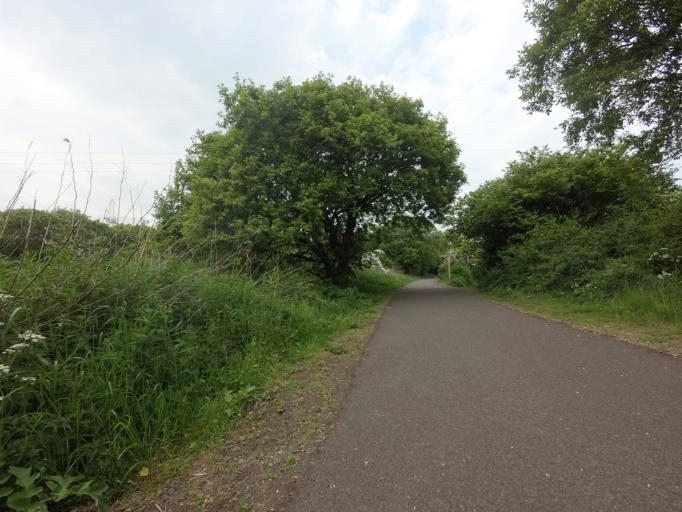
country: GB
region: Scotland
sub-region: Fife
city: Townhill
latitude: 56.0910
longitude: -3.4455
